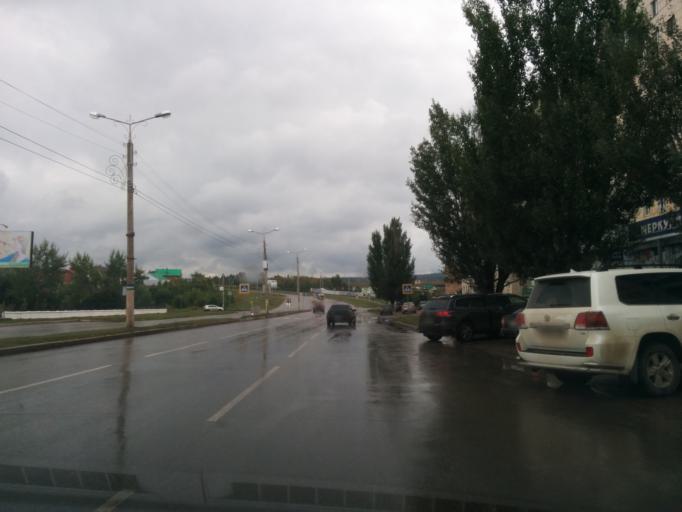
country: RU
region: Bashkortostan
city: Oktyabr'skiy
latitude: 54.4812
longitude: 53.5262
